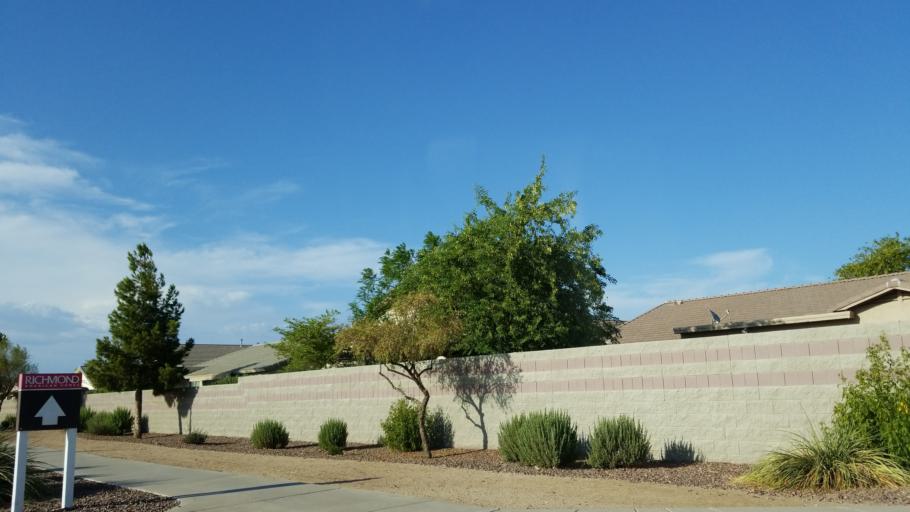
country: US
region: Arizona
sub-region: Maricopa County
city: Laveen
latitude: 33.3785
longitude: -112.2196
